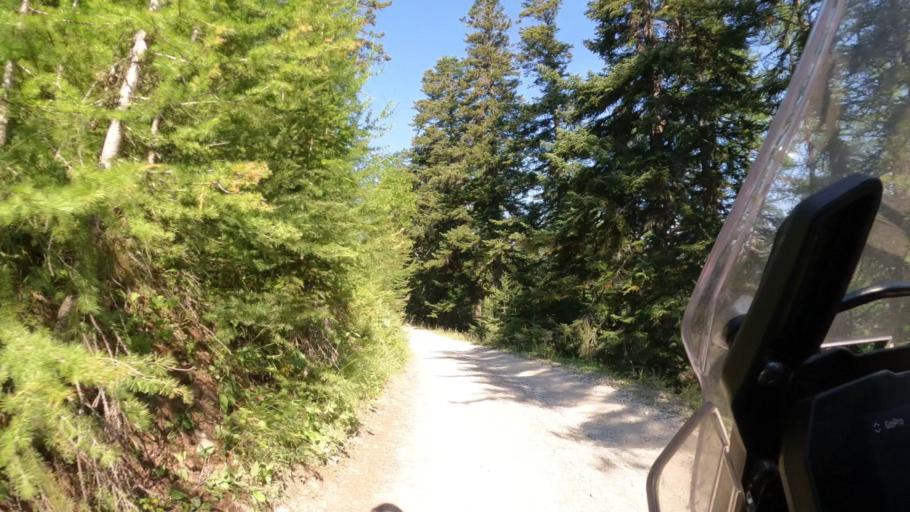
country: FR
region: Provence-Alpes-Cote d'Azur
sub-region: Departement des Hautes-Alpes
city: Embrun
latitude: 44.5946
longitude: 6.5731
